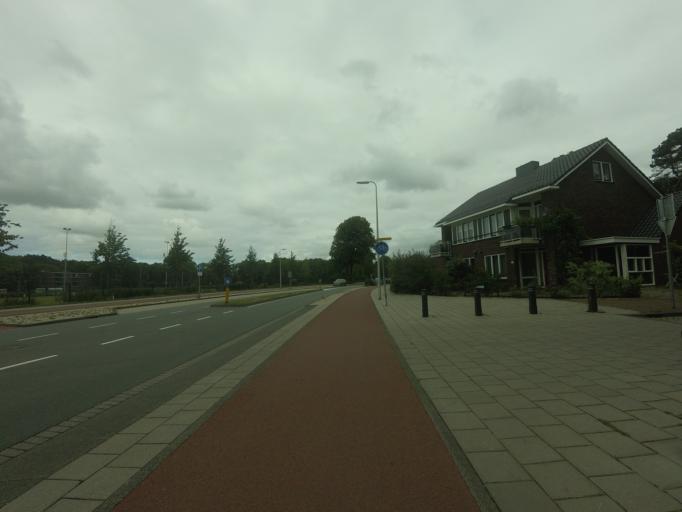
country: NL
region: North Holland
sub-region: Gemeente Bloemendaal
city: Bloemendaal
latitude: 52.4154
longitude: 4.6181
